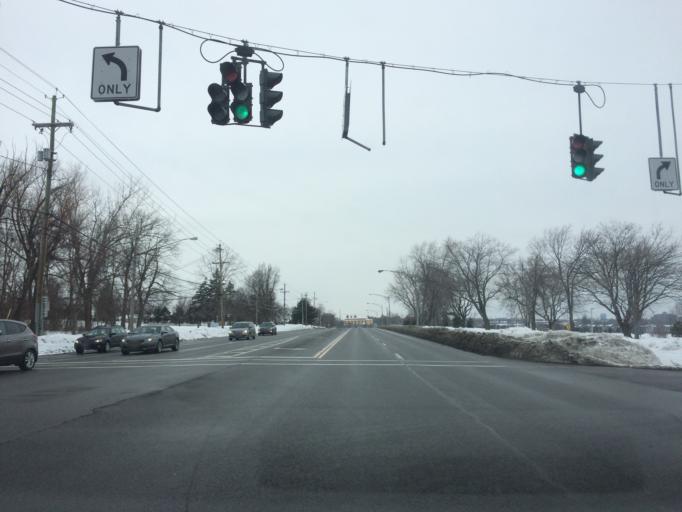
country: US
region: New York
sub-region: Monroe County
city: Rochester
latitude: 43.0980
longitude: -77.6133
